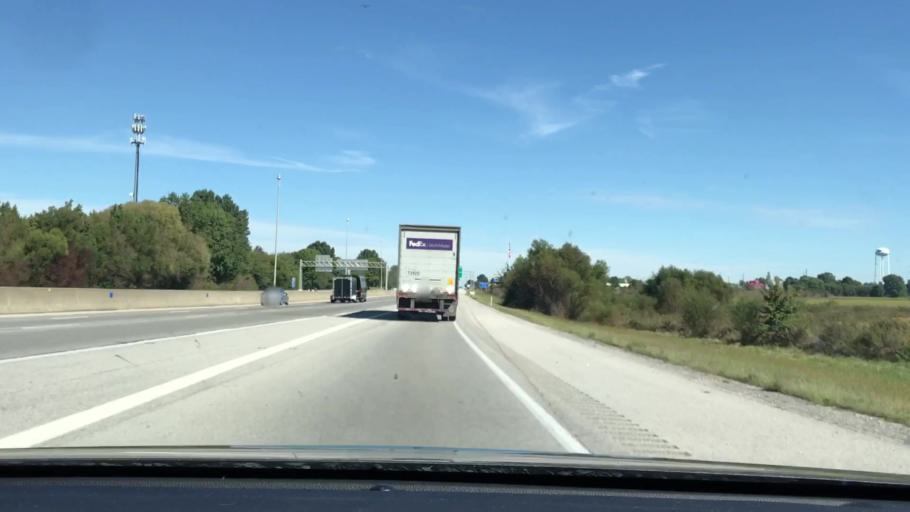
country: US
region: Kentucky
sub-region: Warren County
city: Plano
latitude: 36.9180
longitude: -86.4276
